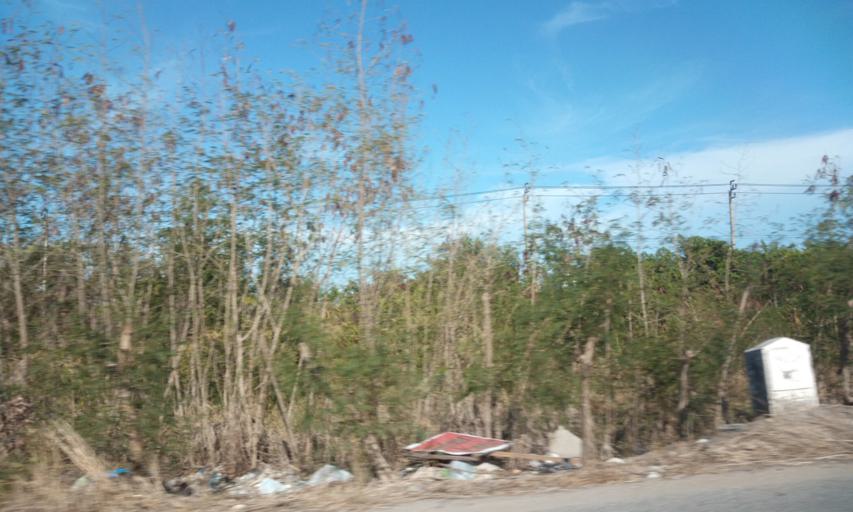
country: TH
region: Samut Prakan
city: Bang Bo District
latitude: 13.5298
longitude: 100.7496
